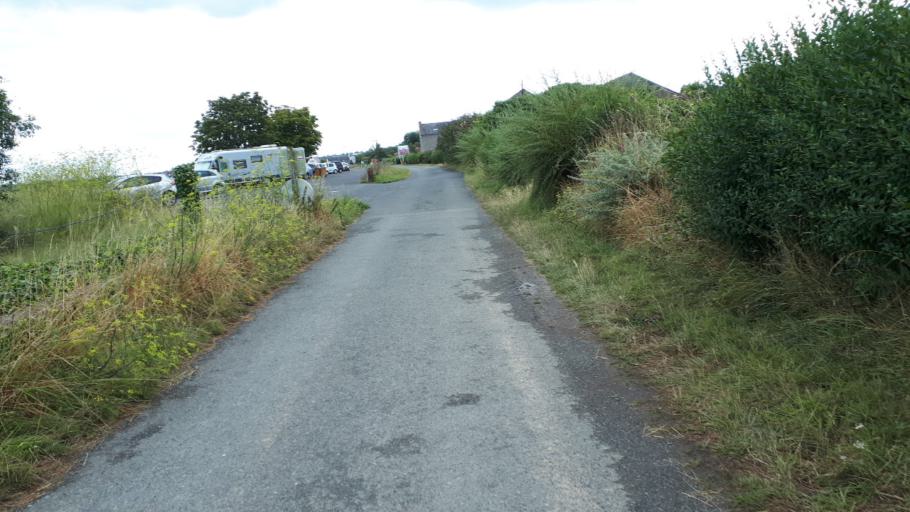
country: FR
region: Brittany
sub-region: Departement des Cotes-d'Armor
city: Langueux
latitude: 48.5059
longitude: -2.6986
